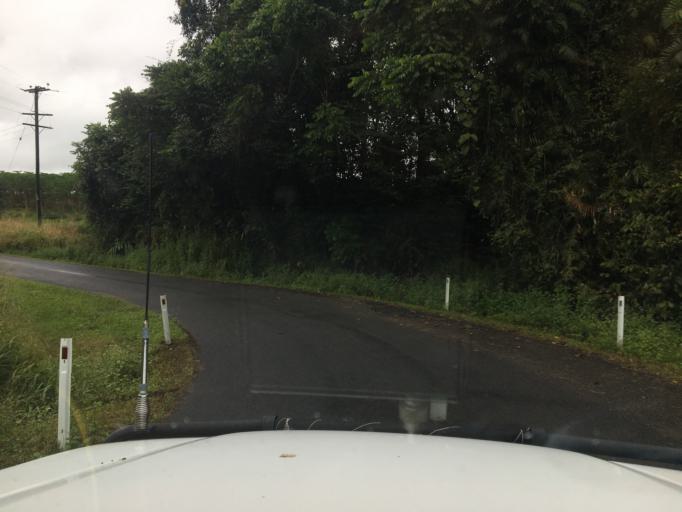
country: AU
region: Queensland
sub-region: Cassowary Coast
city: Innisfail
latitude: -17.4445
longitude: 145.8590
